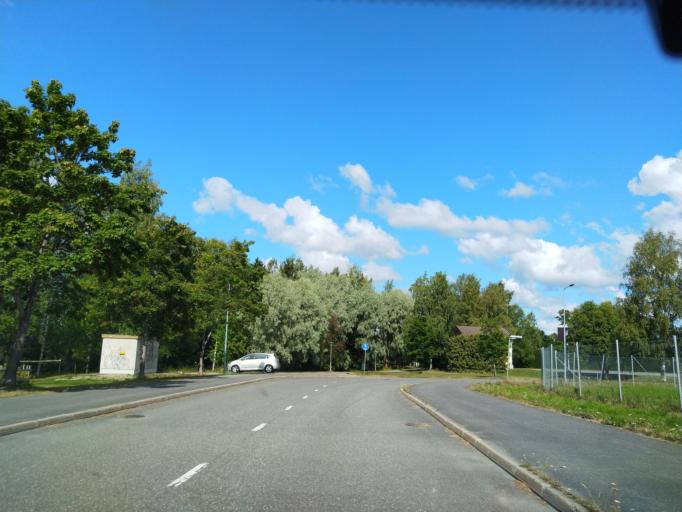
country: FI
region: Satakunta
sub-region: Pori
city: Huittinen
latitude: 61.1761
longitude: 22.6943
